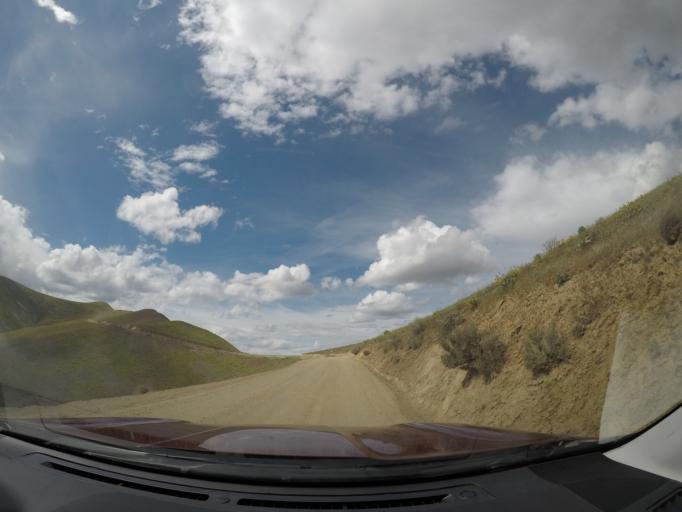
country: US
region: Washington
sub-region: Chelan County
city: West Wenatchee
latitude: 47.4626
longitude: -120.3679
